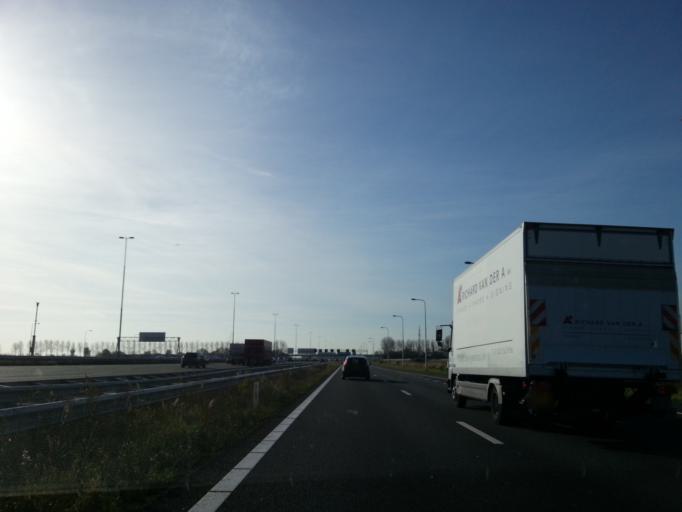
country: NL
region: North Holland
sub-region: Gemeente Haarlemmermeer
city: Hoofddorp
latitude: 52.2719
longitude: 4.7027
